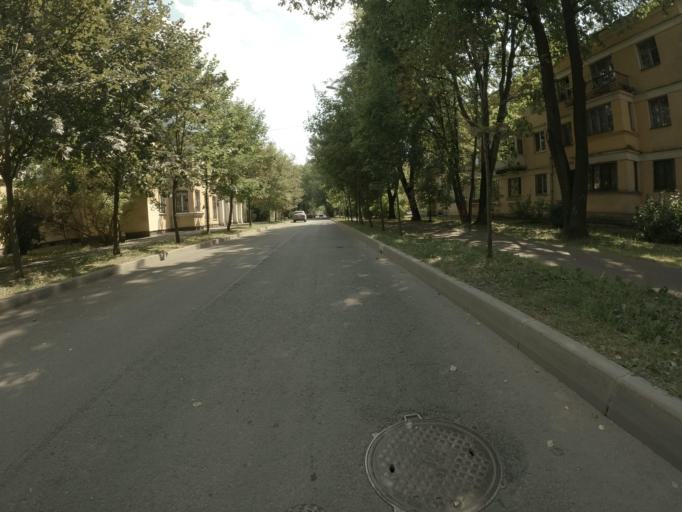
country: RU
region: St.-Petersburg
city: Avtovo
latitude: 59.8957
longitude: 30.2594
